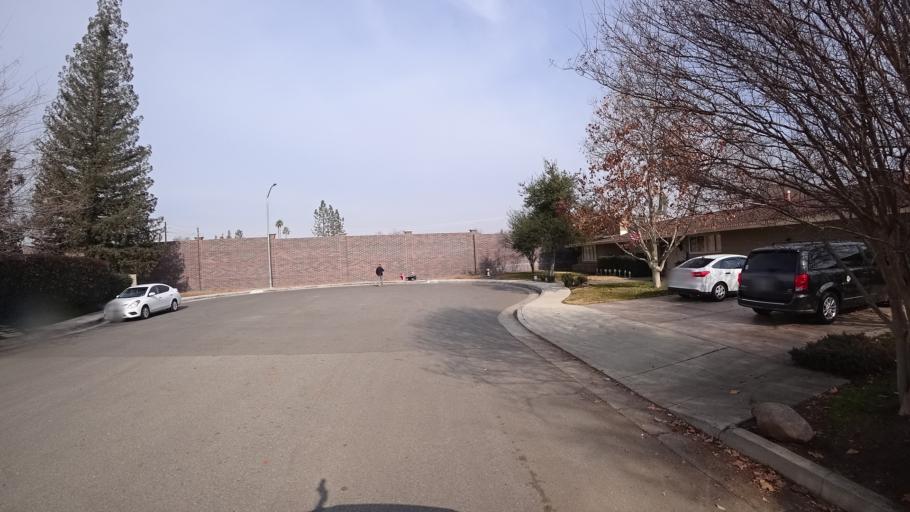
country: US
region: California
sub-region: Kern County
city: Bakersfield
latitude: 35.3805
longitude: -119.0351
